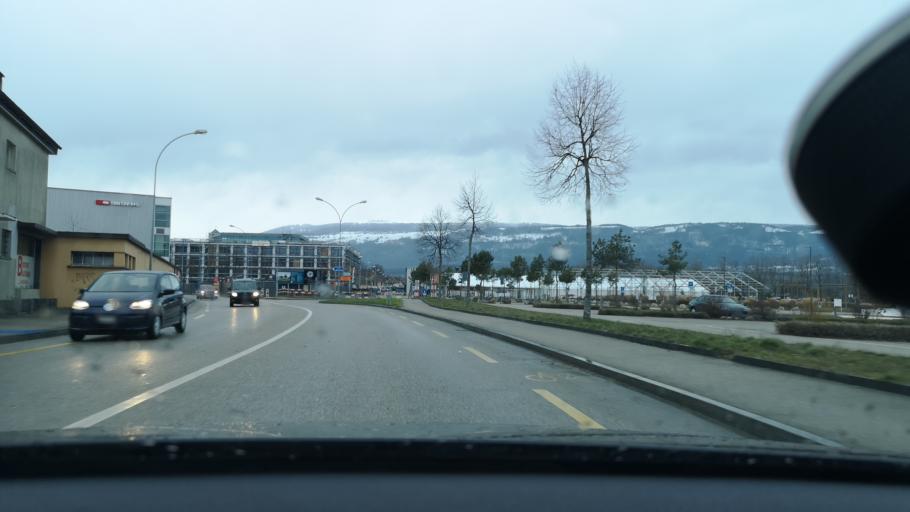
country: CH
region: Vaud
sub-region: Jura-Nord vaudois District
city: Yverdon-les-Bains
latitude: 46.7838
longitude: 6.6441
